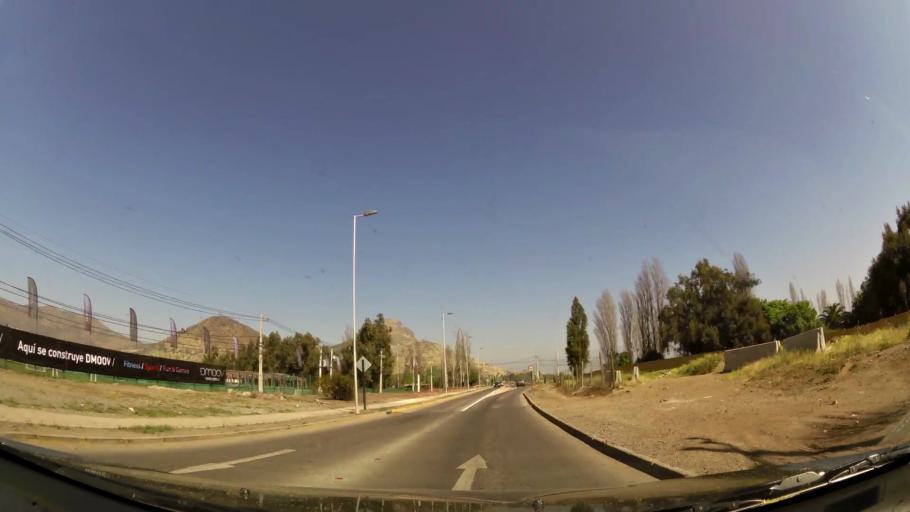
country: CL
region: Santiago Metropolitan
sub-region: Provincia de Chacabuco
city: Chicureo Abajo
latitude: -33.3034
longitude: -70.6674
